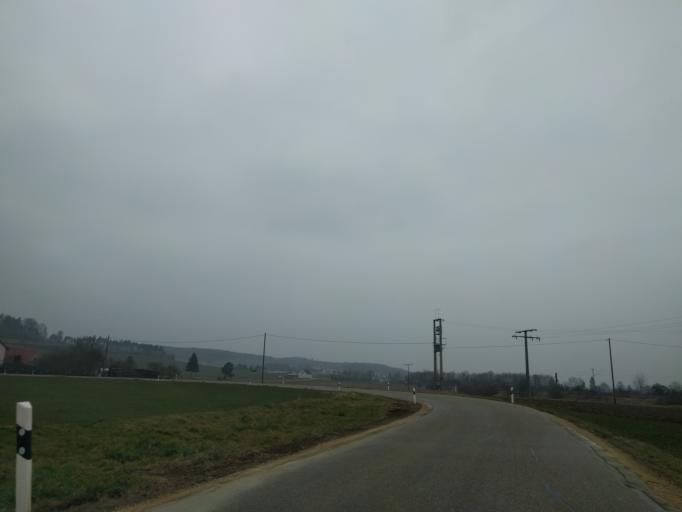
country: DE
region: Bavaria
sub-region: Swabia
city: Donauwoerth
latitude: 48.7226
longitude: 10.7189
